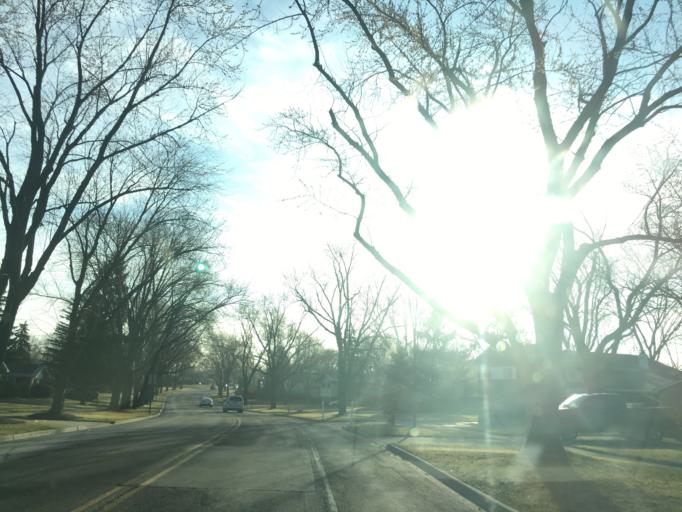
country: US
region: Illinois
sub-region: Cook County
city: Hoffman Estates
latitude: 42.0616
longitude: -88.0976
